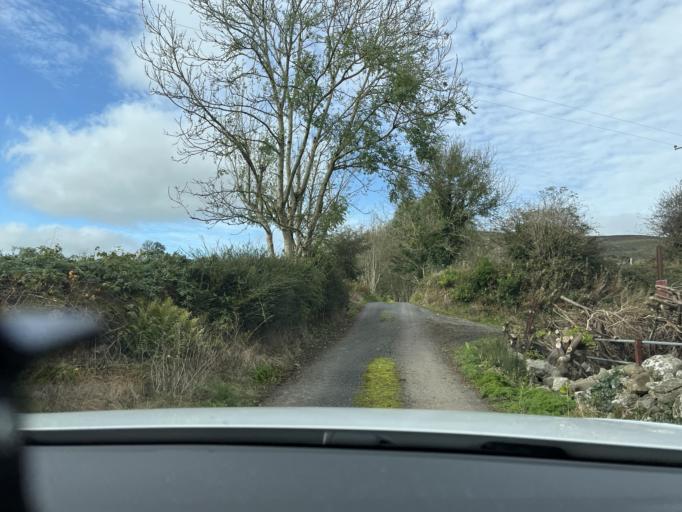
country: IE
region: Connaught
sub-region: Sligo
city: Ballymote
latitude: 54.0463
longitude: -8.4326
